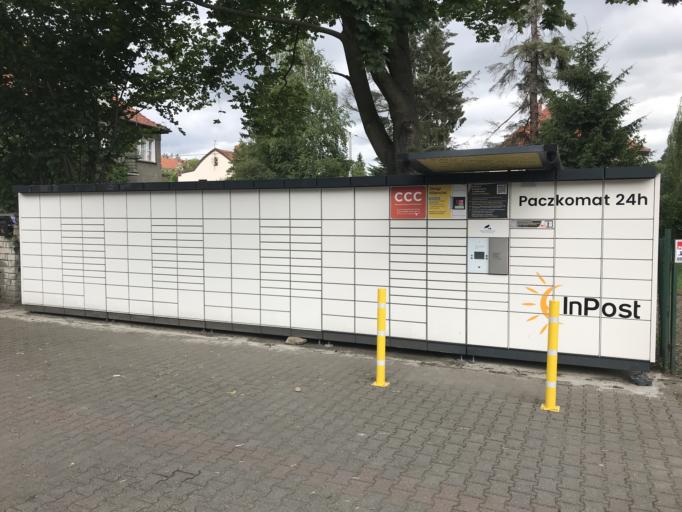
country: PL
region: Lower Silesian Voivodeship
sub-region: Powiat klodzki
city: Polanica-Zdroj
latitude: 50.4023
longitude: 16.5089
